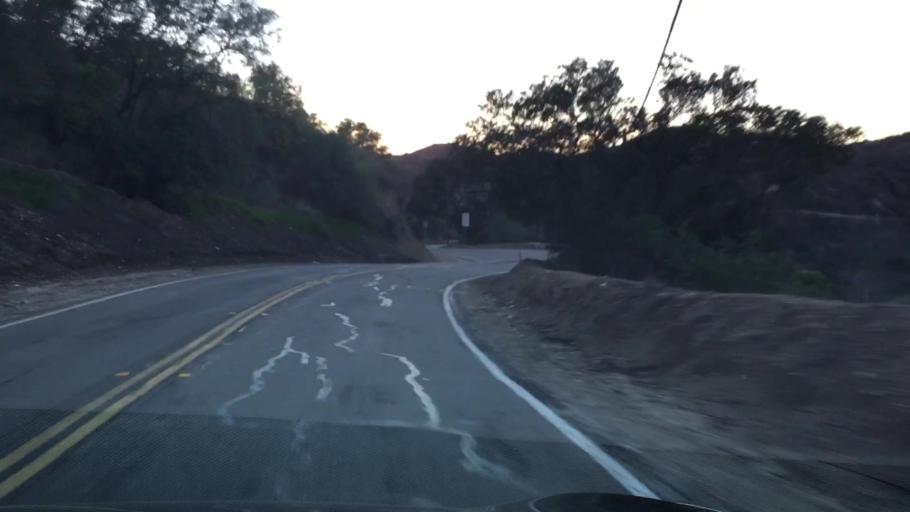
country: US
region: California
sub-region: Los Angeles County
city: Whittier
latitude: 33.9950
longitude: -118.0102
